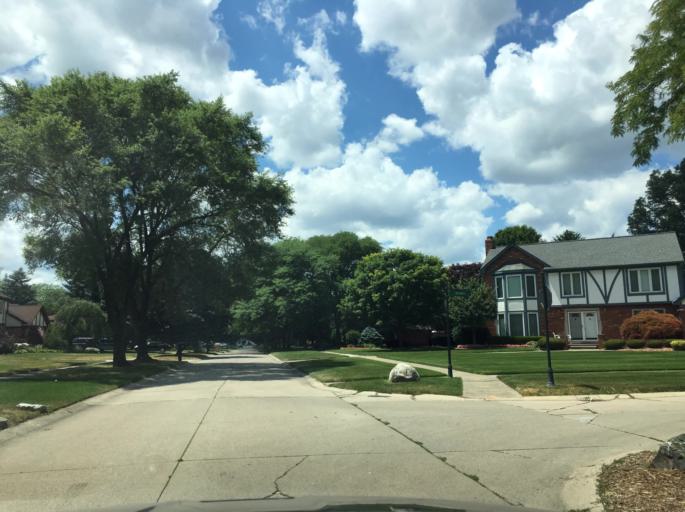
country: US
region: Michigan
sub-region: Macomb County
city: Utica
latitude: 42.6342
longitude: -83.0078
